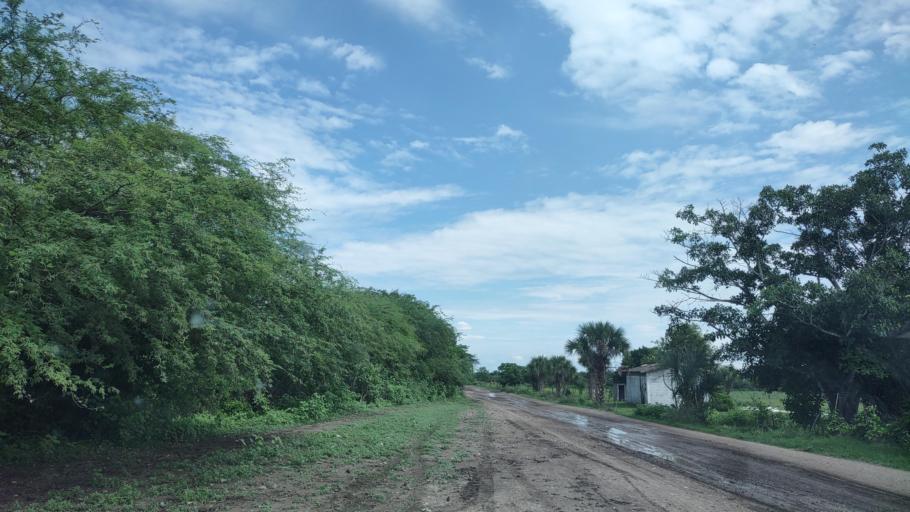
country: MX
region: Veracruz
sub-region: Panuco
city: Oviedo
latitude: 22.0011
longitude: -98.4541
